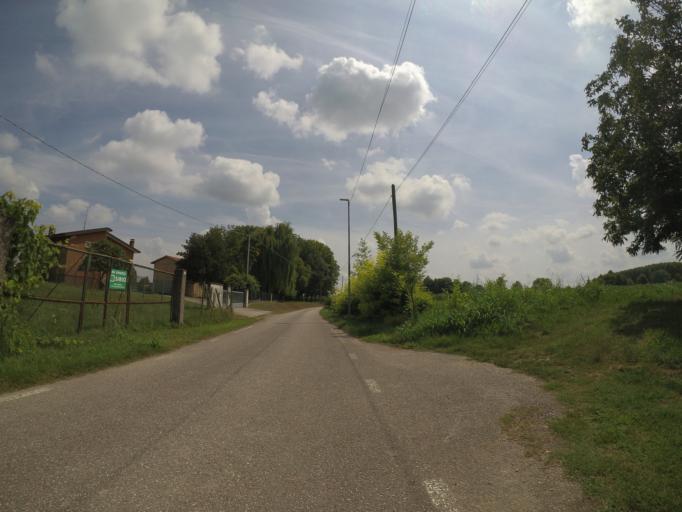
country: IT
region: Friuli Venezia Giulia
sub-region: Provincia di Udine
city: Varmo
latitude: 45.8963
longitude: 13.0182
